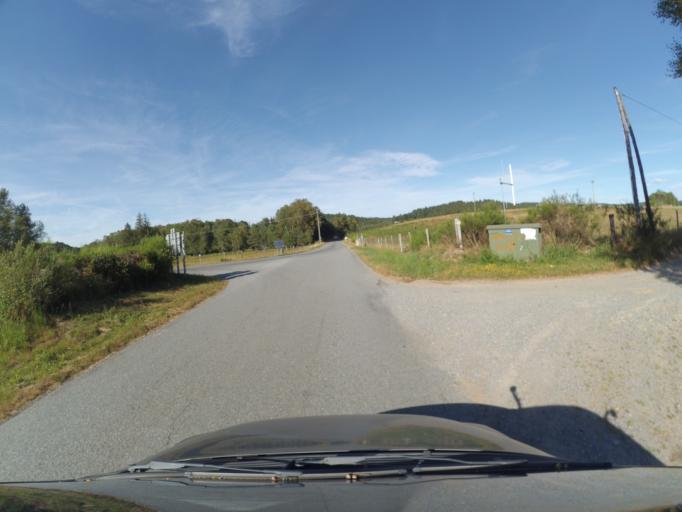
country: FR
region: Limousin
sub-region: Departement de la Correze
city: Bugeat
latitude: 45.7046
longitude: 2.0235
